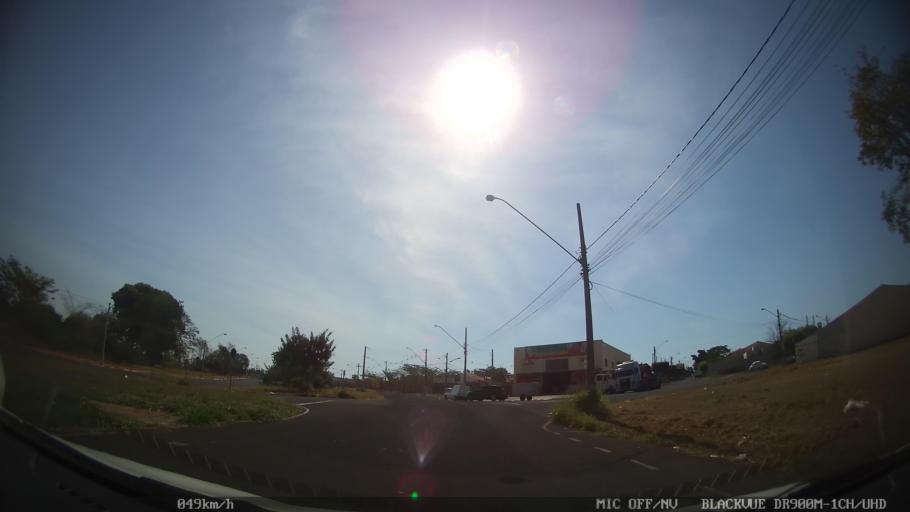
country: BR
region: Sao Paulo
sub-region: Sao Jose Do Rio Preto
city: Sao Jose do Rio Preto
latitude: -20.7854
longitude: -49.4247
